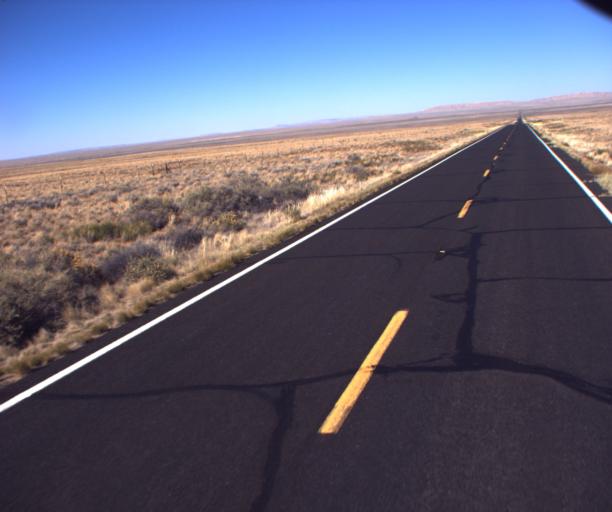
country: US
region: Arizona
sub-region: Navajo County
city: First Mesa
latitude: 35.6499
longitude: -110.4891
